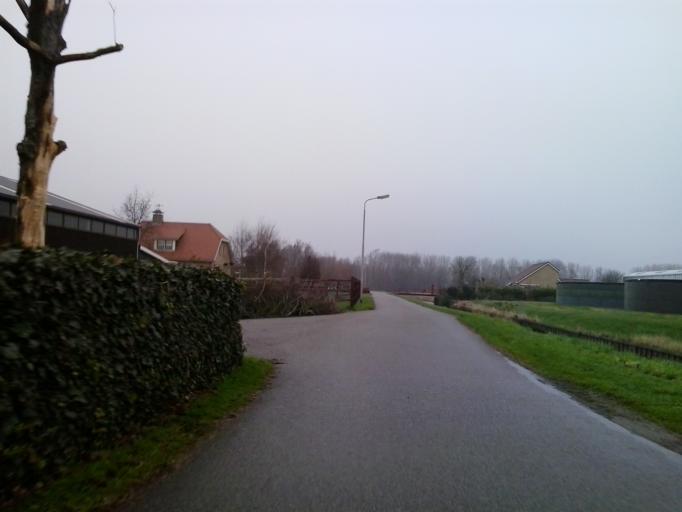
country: NL
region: South Holland
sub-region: Gemeente Pijnacker-Nootdorp
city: Pijnacker
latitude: 52.0199
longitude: 4.4192
